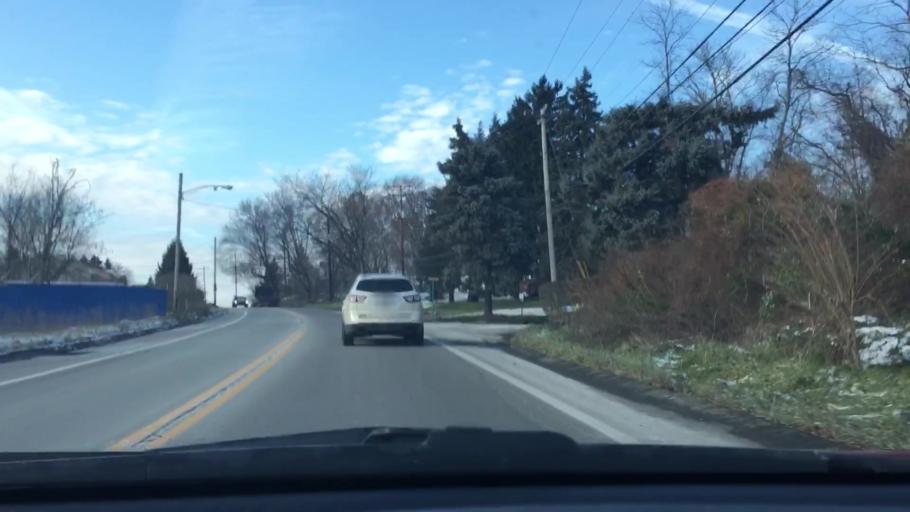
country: US
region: Pennsylvania
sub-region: Allegheny County
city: Glassport
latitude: 40.3418
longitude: -79.9163
